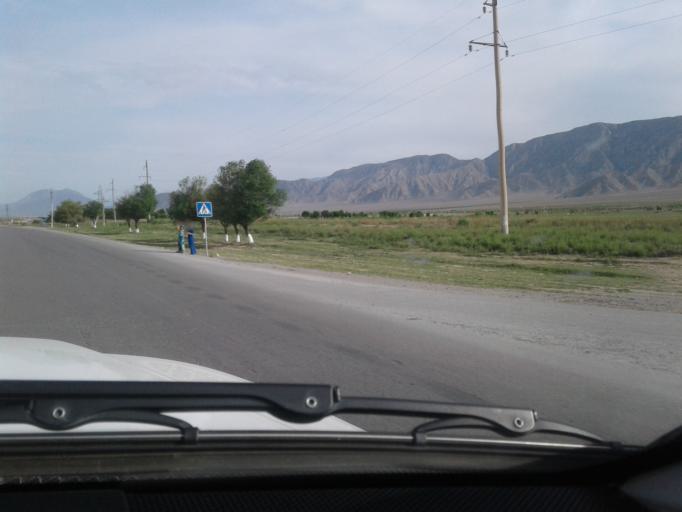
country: TM
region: Ahal
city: Arcabil
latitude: 38.1926
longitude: 57.8400
